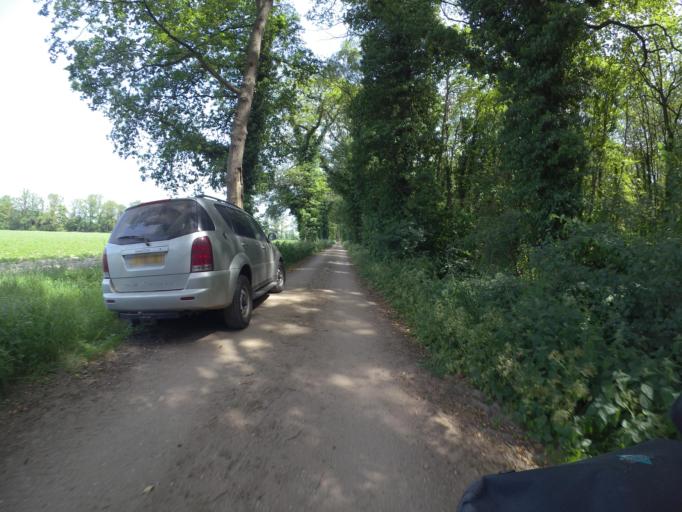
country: NL
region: Gelderland
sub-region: Gemeente Aalten
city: Aalten
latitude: 51.9409
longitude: 6.5319
